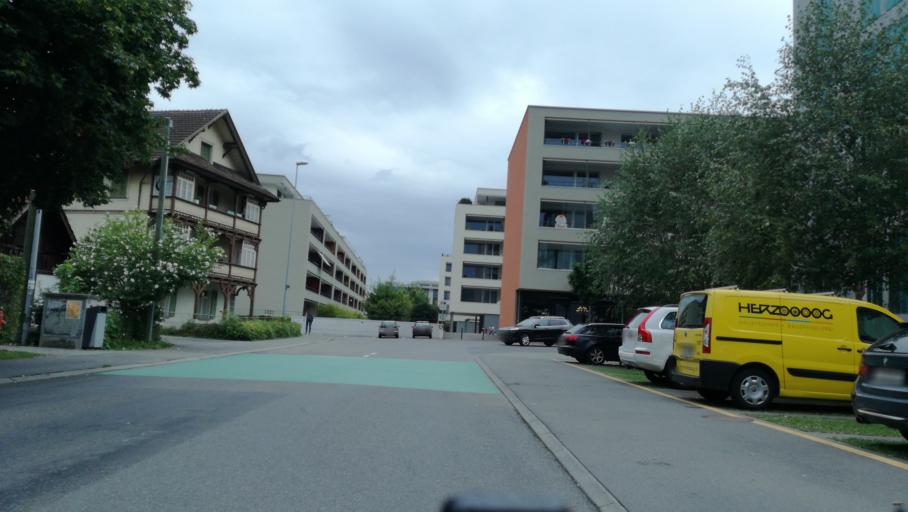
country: CH
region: Lucerne
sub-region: Lucerne-Land District
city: Ebikon
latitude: 47.0836
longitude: 8.3425
